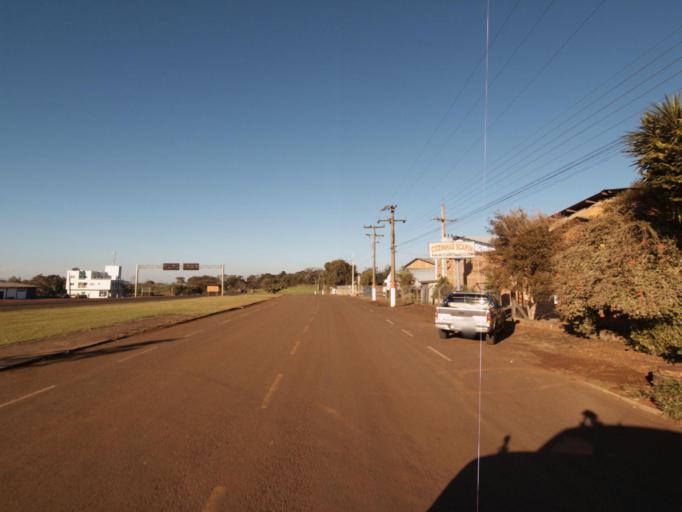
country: BR
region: Santa Catarina
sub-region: Chapeco
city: Chapeco
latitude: -26.9058
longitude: -52.9011
